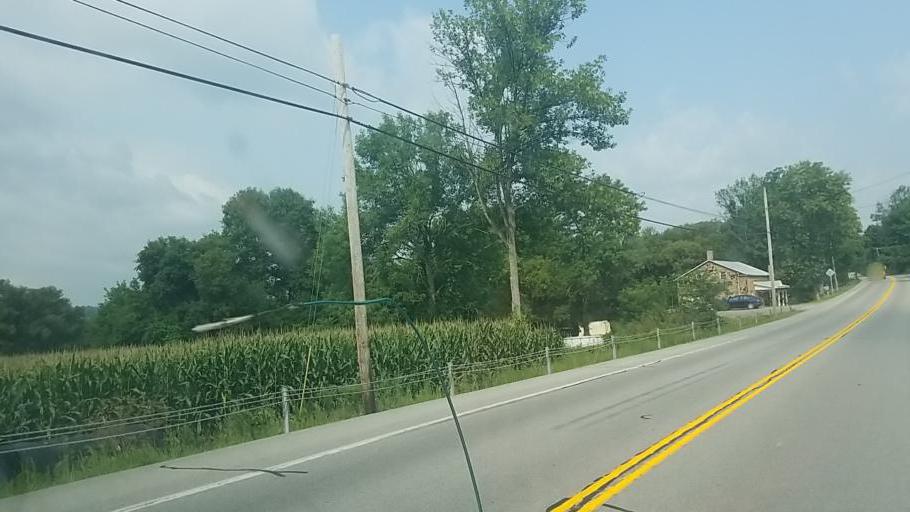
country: US
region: New York
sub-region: Montgomery County
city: Fort Plain
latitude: 42.9765
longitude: -74.6370
